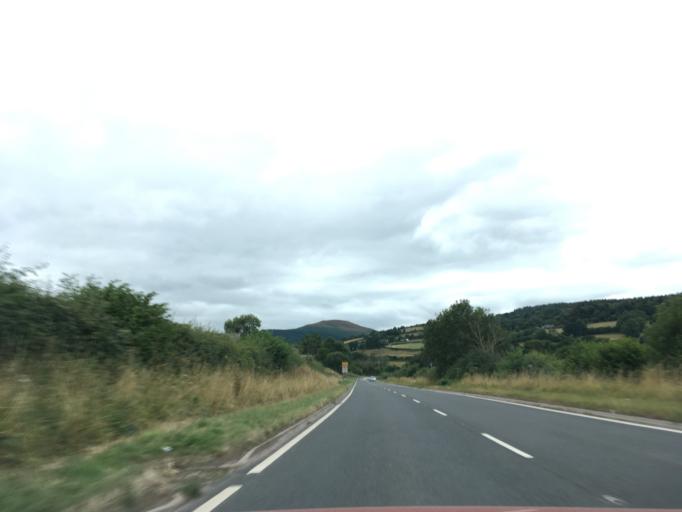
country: GB
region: Wales
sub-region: Blaenau Gwent
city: Brynmawr
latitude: 51.8849
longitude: -3.2234
